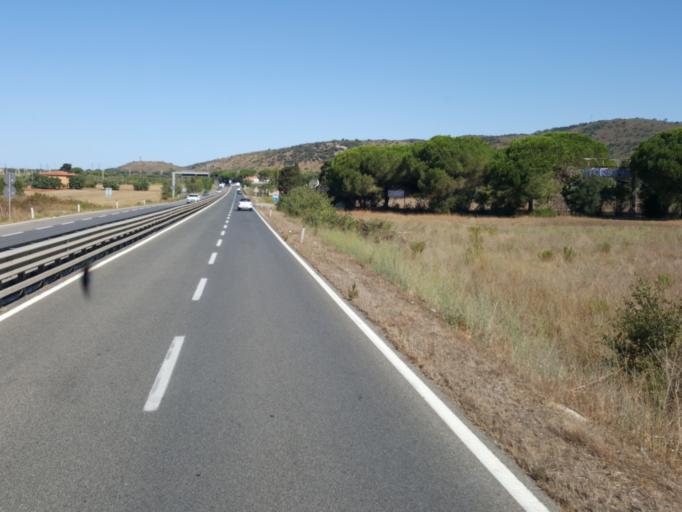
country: IT
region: Tuscany
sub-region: Provincia di Grosseto
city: Orbetello Scalo
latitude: 42.4316
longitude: 11.2842
